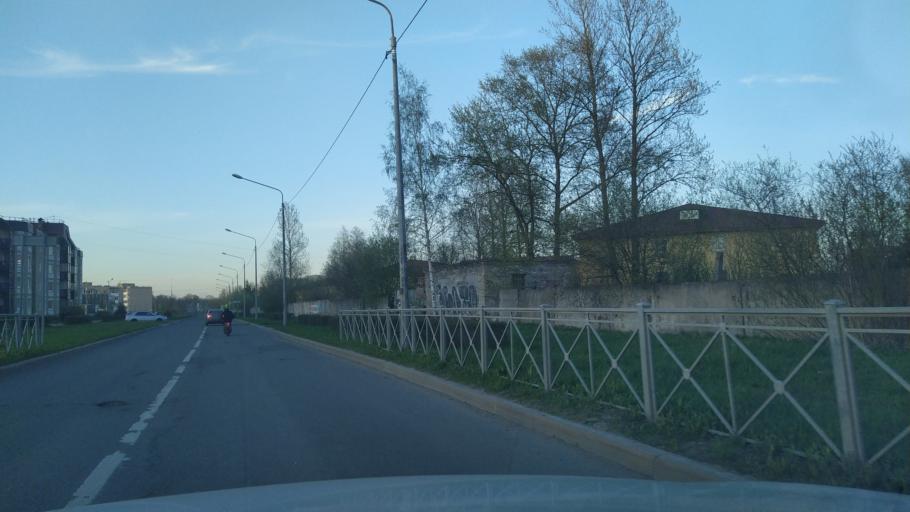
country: RU
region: St.-Petersburg
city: Pushkin
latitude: 59.7016
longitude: 30.3820
